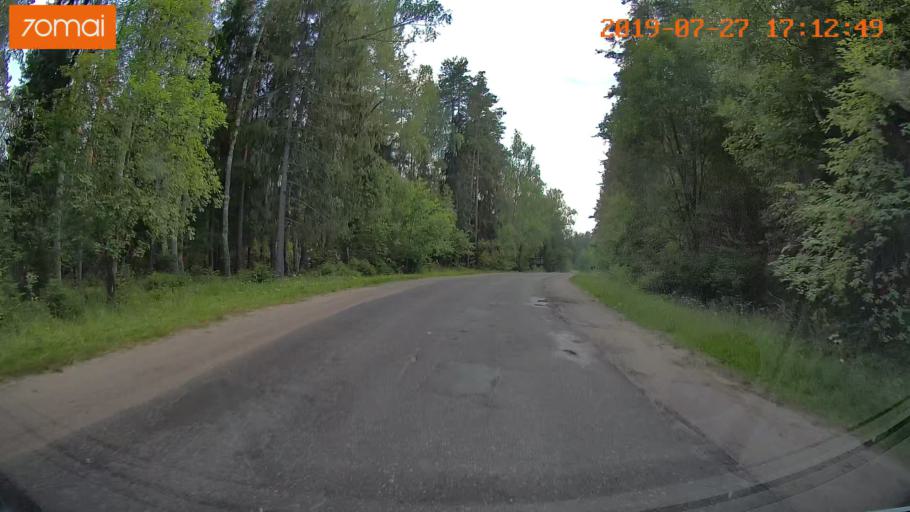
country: RU
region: Ivanovo
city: Novo-Talitsy
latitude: 57.0554
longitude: 40.8587
